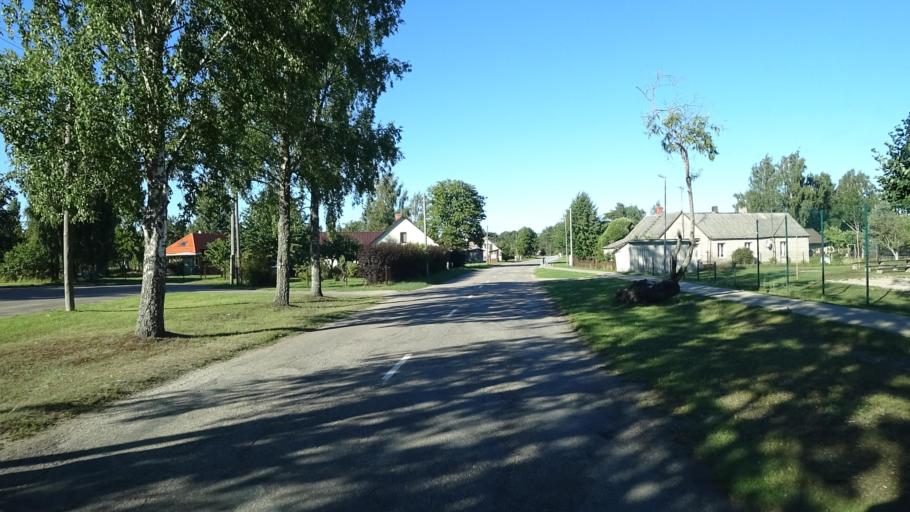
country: LV
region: Dundaga
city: Dundaga
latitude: 57.7450
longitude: 22.5881
